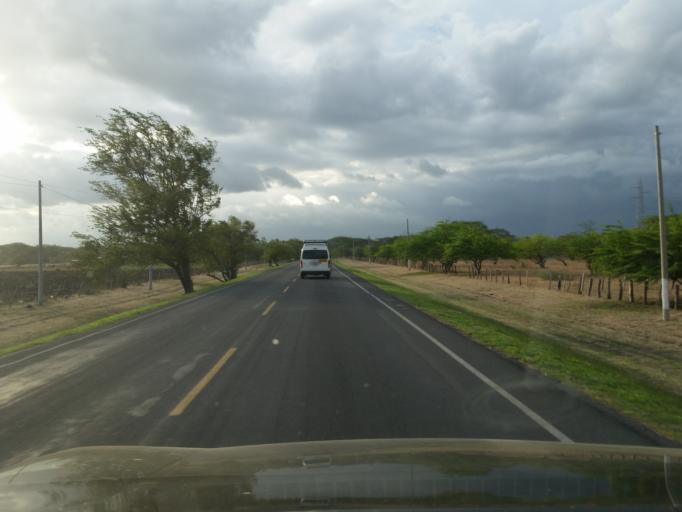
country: NI
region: Granada
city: Nandaime
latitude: 11.6940
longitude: -85.9967
